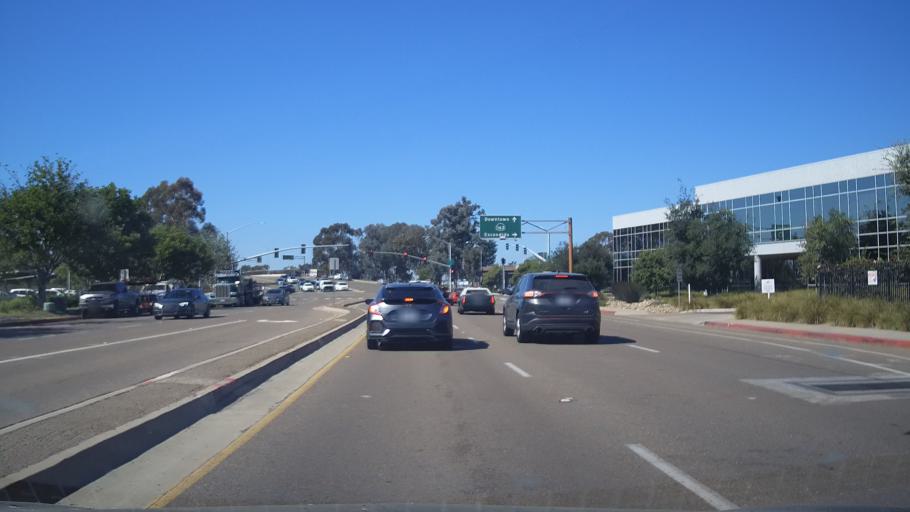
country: US
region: California
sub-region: San Diego County
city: San Diego
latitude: 32.8213
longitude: -117.1431
